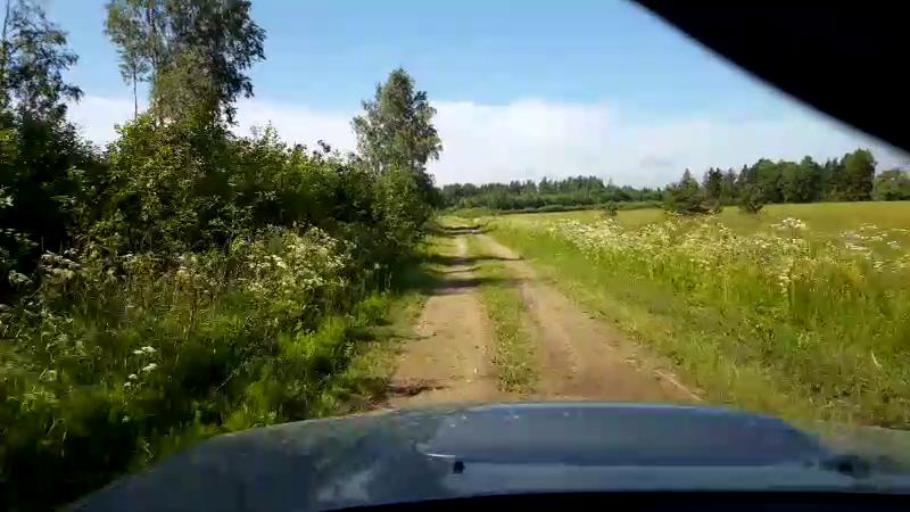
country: EE
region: Paernumaa
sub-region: Sindi linn
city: Sindi
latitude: 58.5064
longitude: 24.6440
